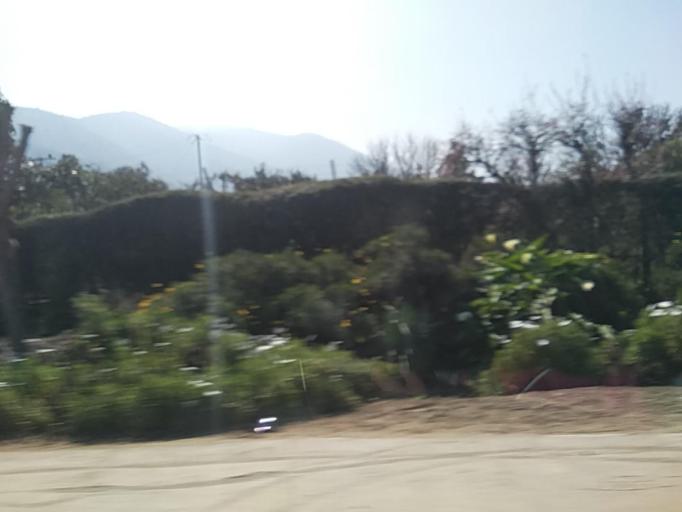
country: CL
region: Santiago Metropolitan
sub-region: Provincia de Chacabuco
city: Lampa
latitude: -33.4079
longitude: -71.0701
